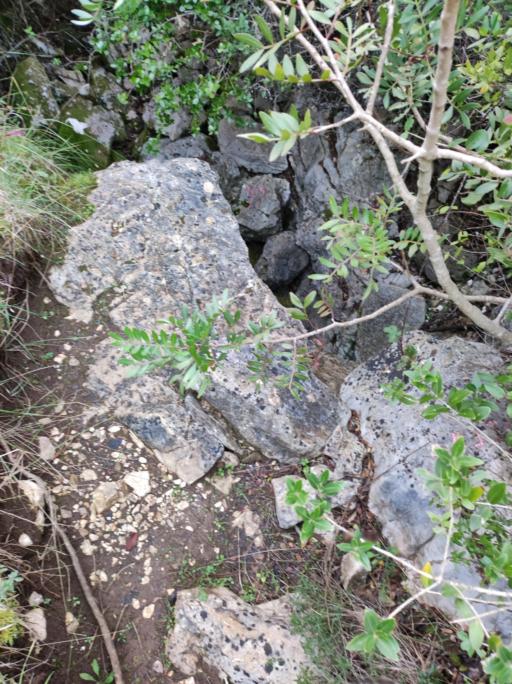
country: FR
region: Provence-Alpes-Cote d'Azur
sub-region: Departement des Alpes-Maritimes
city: Le Rouret
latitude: 43.6726
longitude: 7.0595
